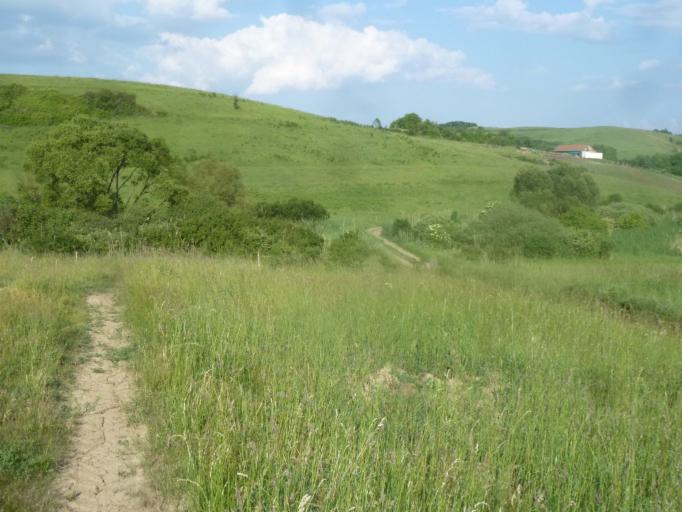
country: HU
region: Borsod-Abauj-Zemplen
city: Putnok
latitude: 48.3760
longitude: 20.4200
